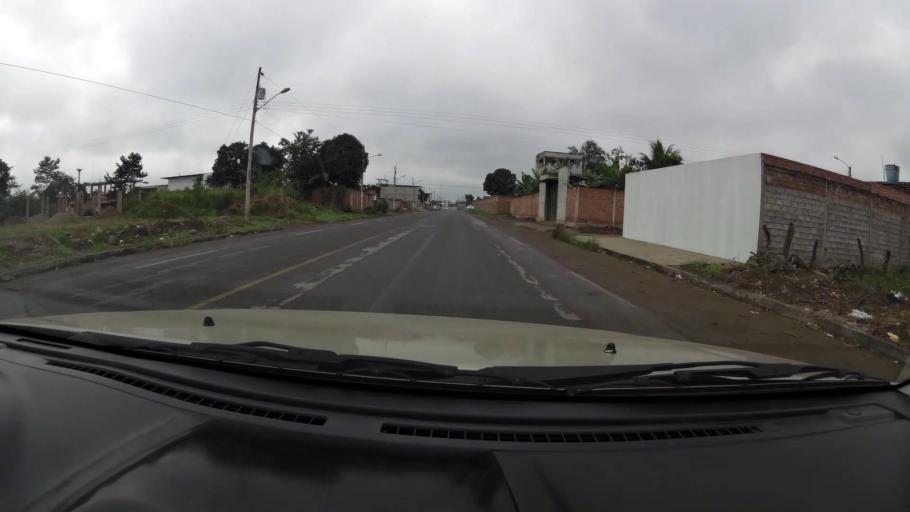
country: EC
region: El Oro
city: Pasaje
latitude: -3.3259
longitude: -79.8220
